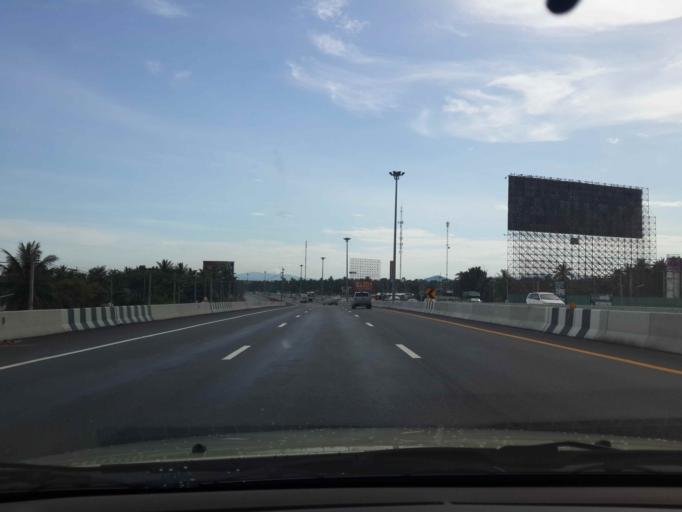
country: TH
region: Chon Buri
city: Ban Talat Bueng
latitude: 13.0081
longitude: 100.9952
